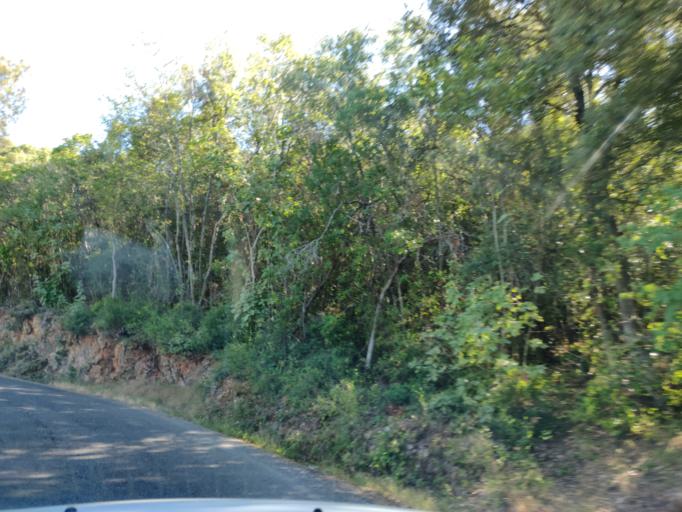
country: IT
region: Tuscany
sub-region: Provincia di Grosseto
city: Monte Argentario
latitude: 42.4215
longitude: 11.1613
